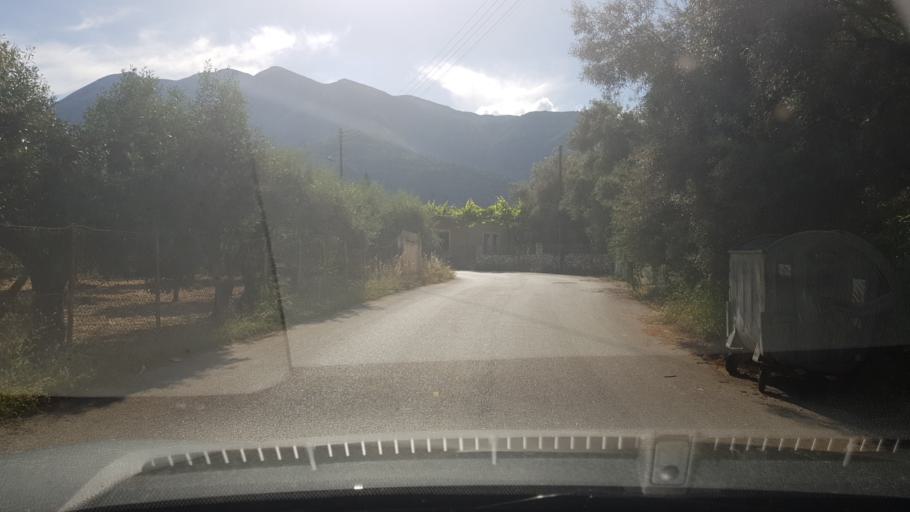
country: GR
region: Ionian Islands
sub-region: Lefkada
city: Nidri
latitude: 38.7113
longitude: 20.7061
